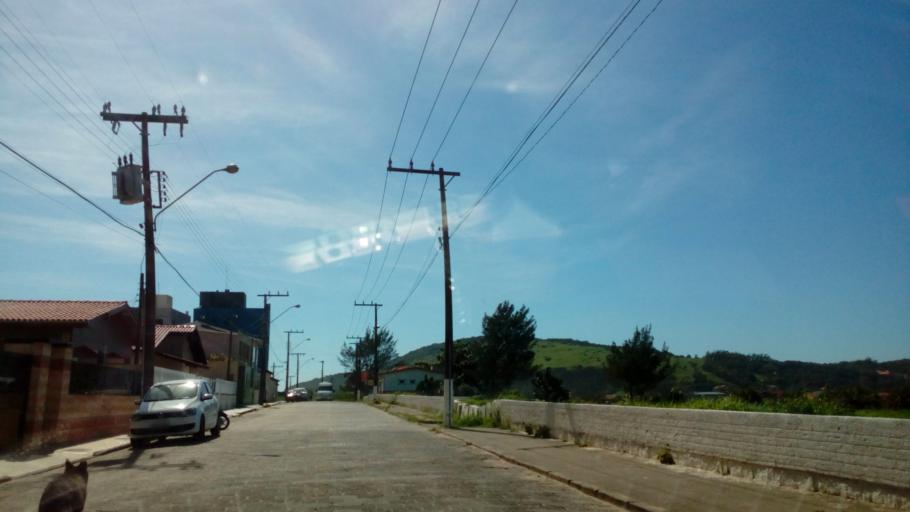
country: BR
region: Santa Catarina
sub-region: Laguna
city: Laguna
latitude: -28.4952
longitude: -48.7649
